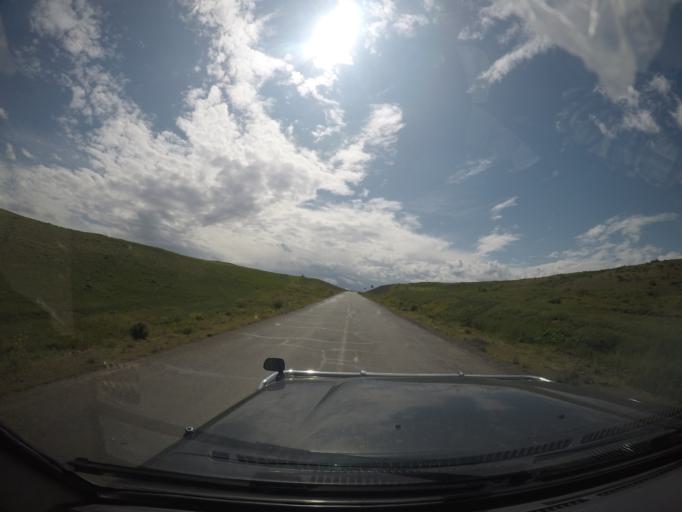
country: MN
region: Hentiy
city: Bayanbulag
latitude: 47.4446
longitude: 109.7688
